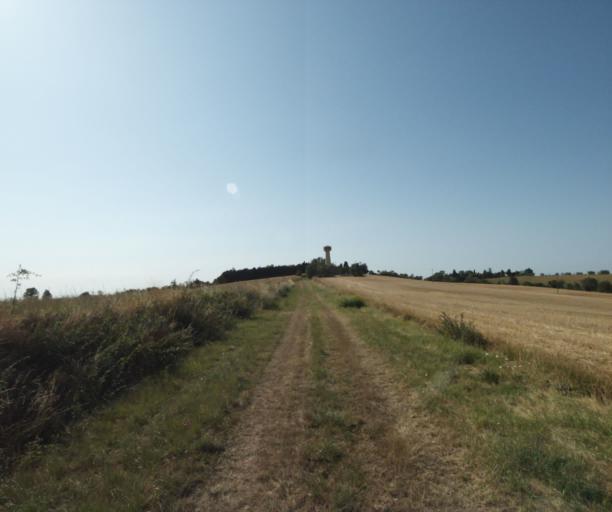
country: FR
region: Midi-Pyrenees
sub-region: Departement de la Haute-Garonne
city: Avignonet-Lauragais
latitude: 43.4234
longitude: 1.8223
